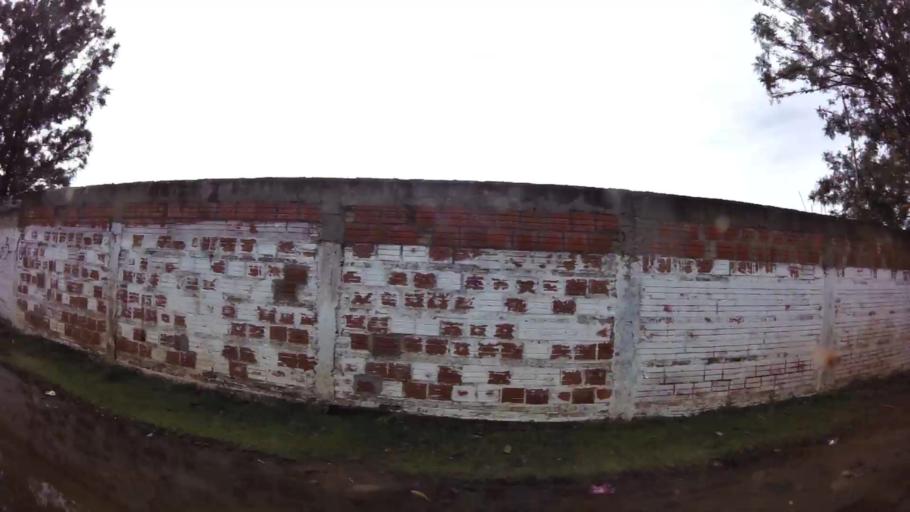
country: PY
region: Central
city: Limpio
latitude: -25.1429
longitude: -57.4727
